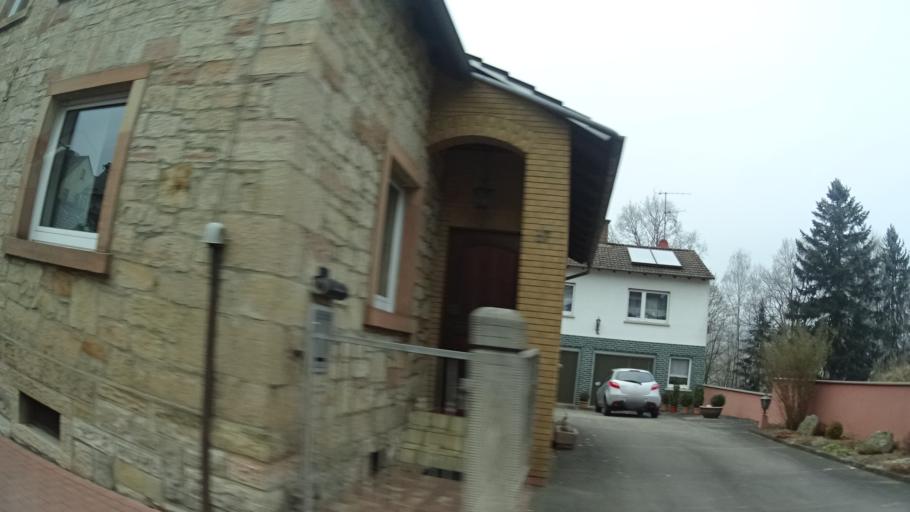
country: DE
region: Bavaria
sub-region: Regierungsbezirk Unterfranken
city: Blankenbach
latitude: 50.0655
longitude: 9.2353
